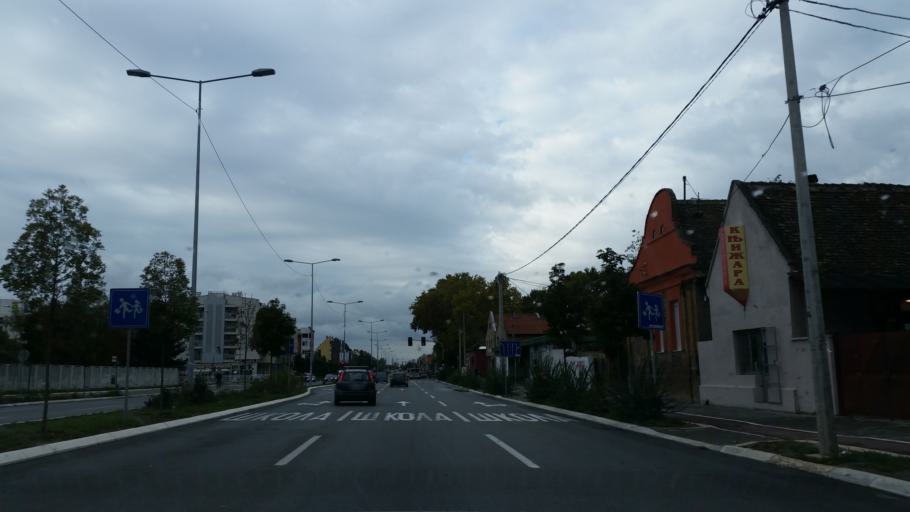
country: RS
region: Central Serbia
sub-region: Belgrade
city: Zemun
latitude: 44.8085
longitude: 20.3777
